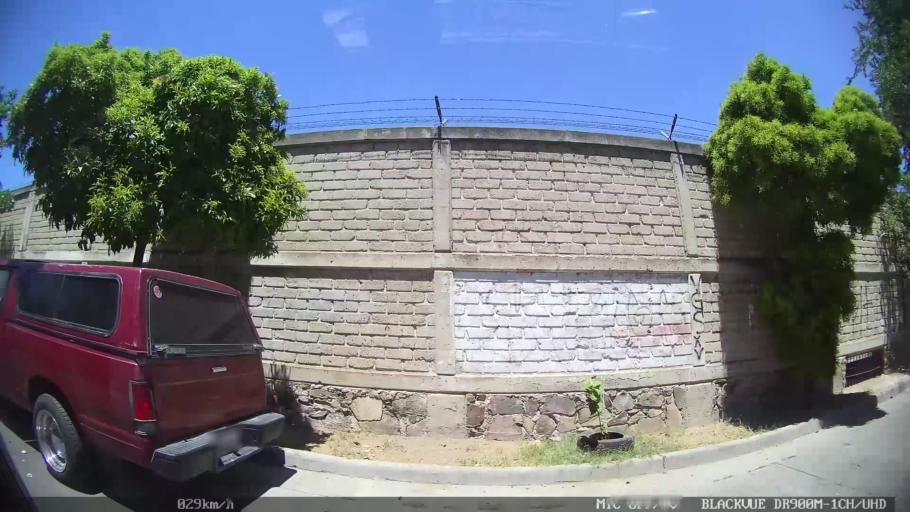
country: MX
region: Jalisco
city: Tlaquepaque
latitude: 20.6562
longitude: -103.2771
